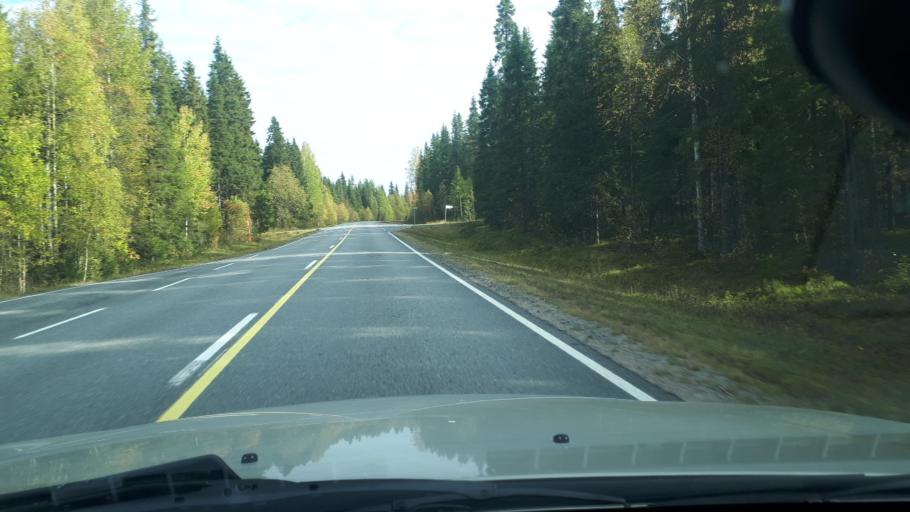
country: FI
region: Northern Ostrobothnia
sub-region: Oulu
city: Yli-Ii
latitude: 65.9494
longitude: 25.9077
